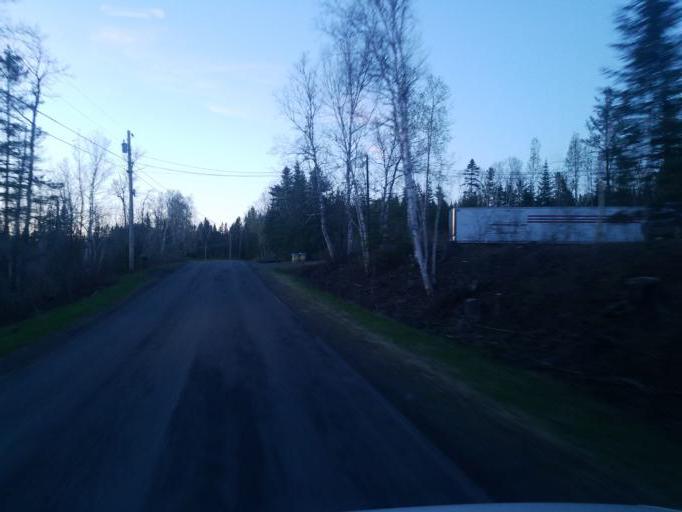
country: US
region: Maine
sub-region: Aroostook County
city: Caribou
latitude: 46.8660
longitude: -68.0710
